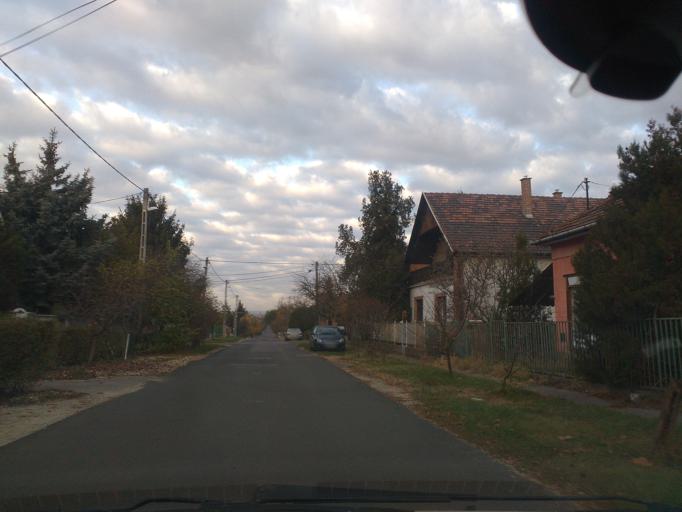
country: HU
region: Budapest
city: Budapest XVIII. keruelet
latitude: 47.4335
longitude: 19.2121
